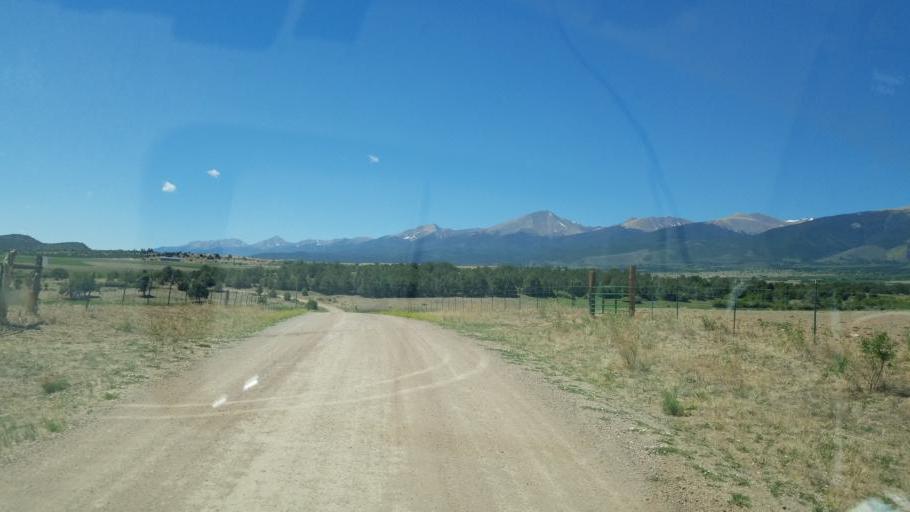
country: US
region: Colorado
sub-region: Custer County
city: Westcliffe
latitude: 38.3015
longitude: -105.6154
